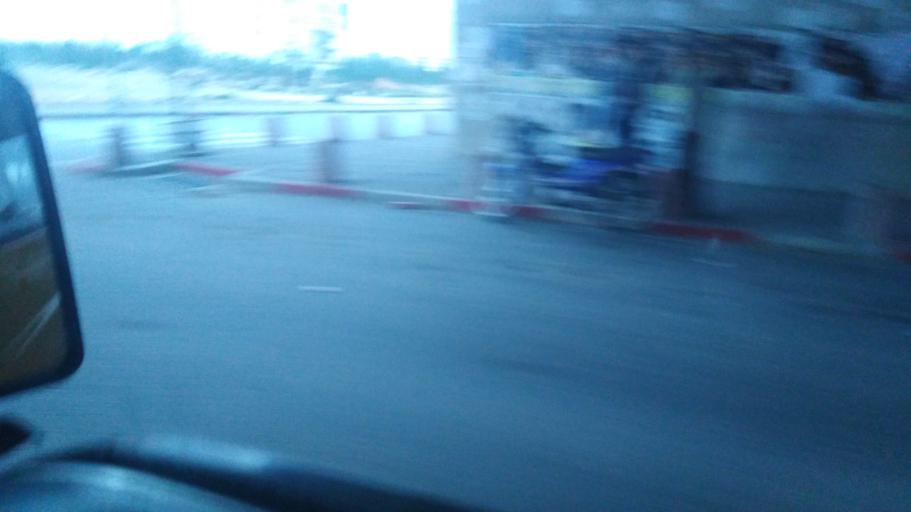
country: TN
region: Susah
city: Sousse
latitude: 35.8029
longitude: 10.6146
